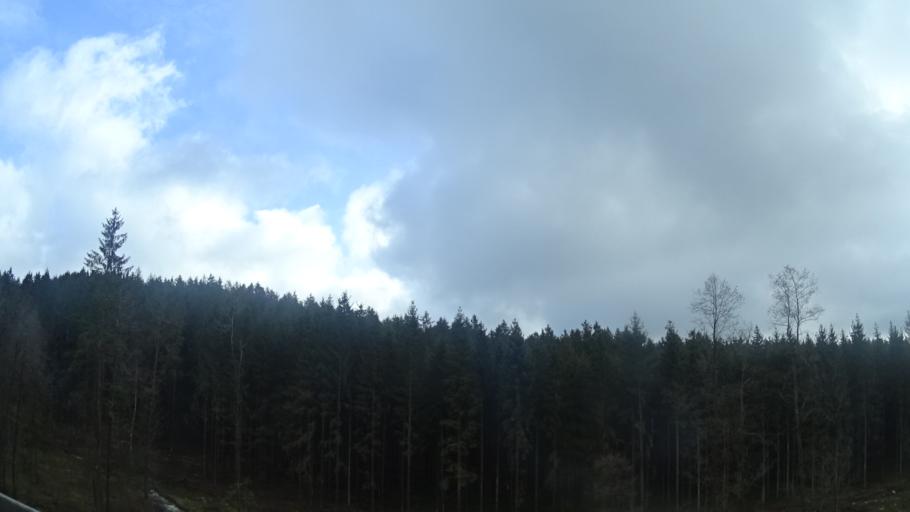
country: DE
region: Rheinland-Pfalz
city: Borfink
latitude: 49.6950
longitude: 7.0812
